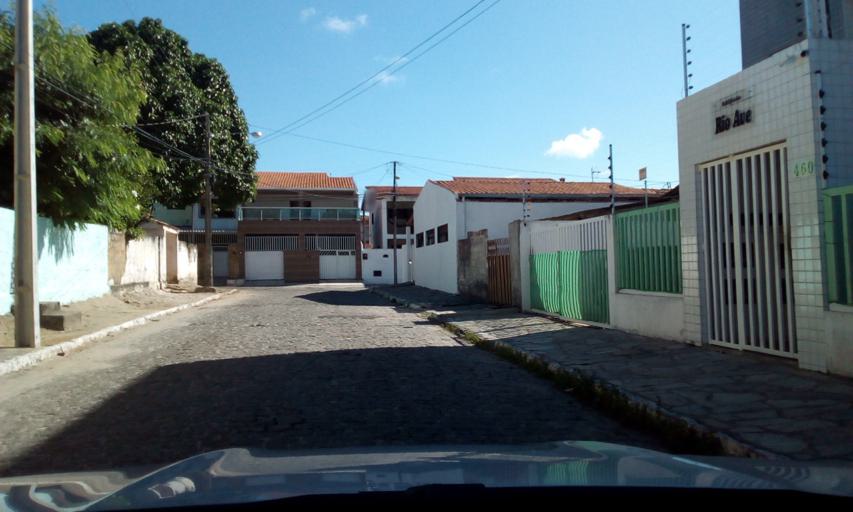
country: BR
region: Paraiba
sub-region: Joao Pessoa
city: Joao Pessoa
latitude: -7.1773
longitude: -34.8421
